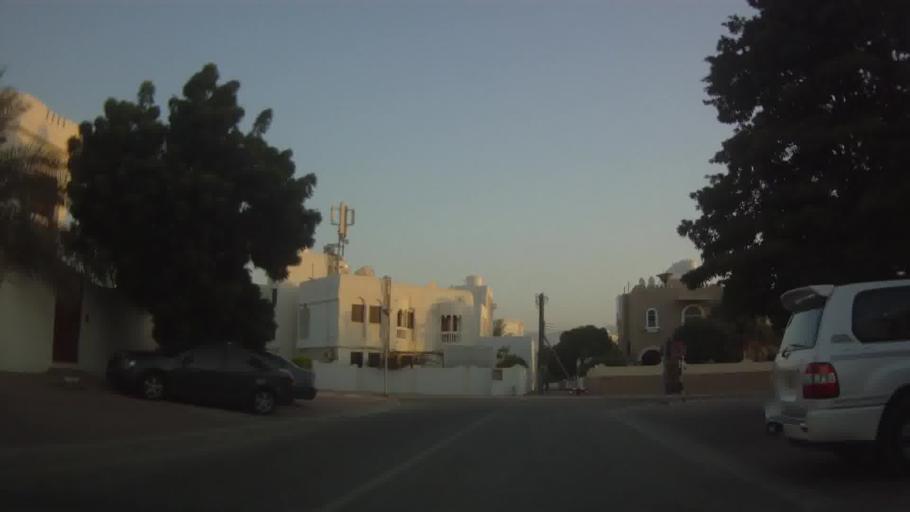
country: OM
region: Muhafazat Masqat
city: Bawshar
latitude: 23.6025
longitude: 58.4054
